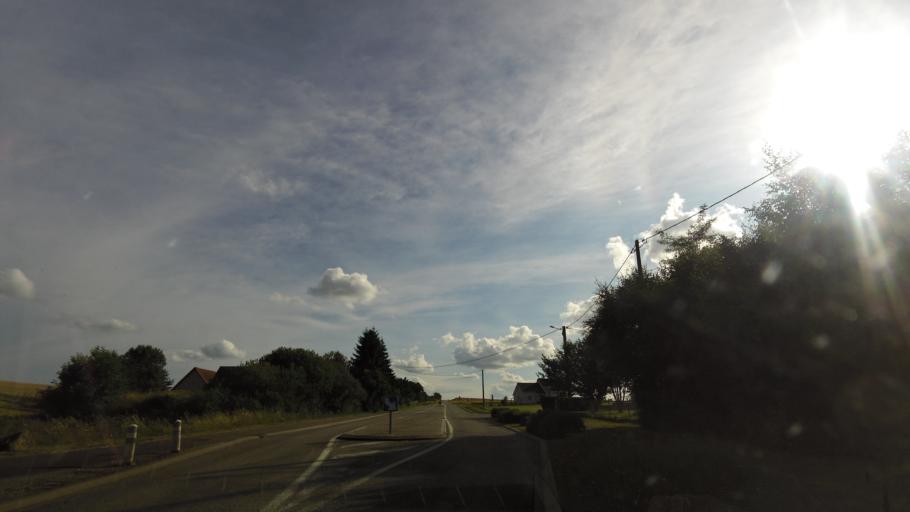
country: FR
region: Lorraine
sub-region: Departement de la Moselle
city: Lorquin
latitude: 48.7094
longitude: 6.9945
